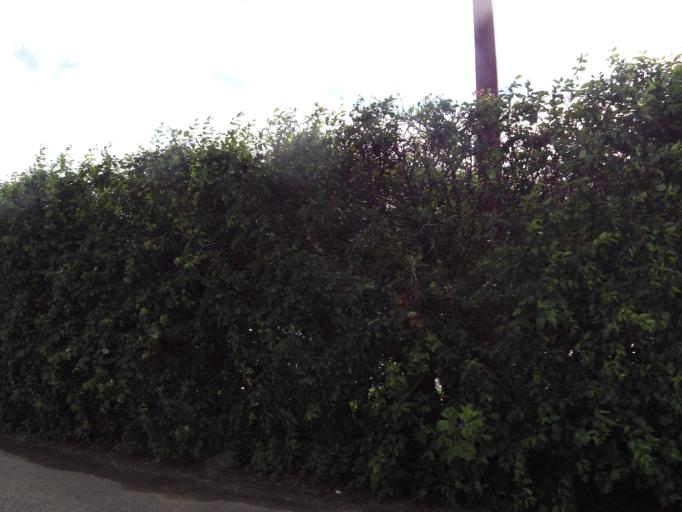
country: US
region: Minnesota
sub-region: Olmsted County
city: Rochester
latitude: 44.0039
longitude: -92.4589
